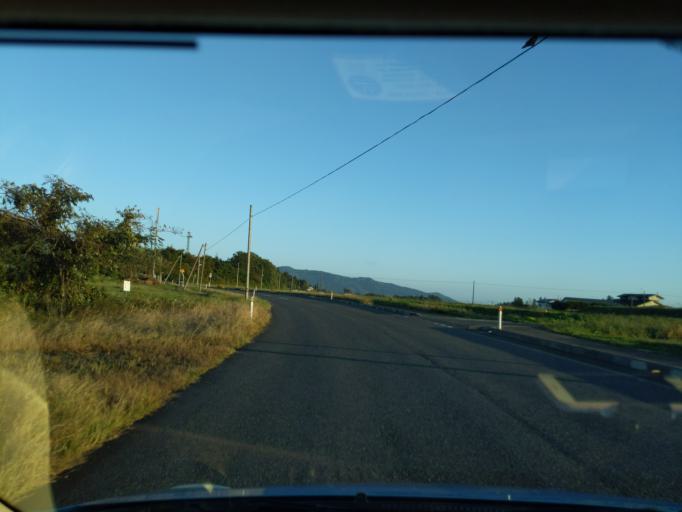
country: JP
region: Iwate
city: Mizusawa
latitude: 39.0687
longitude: 141.0963
